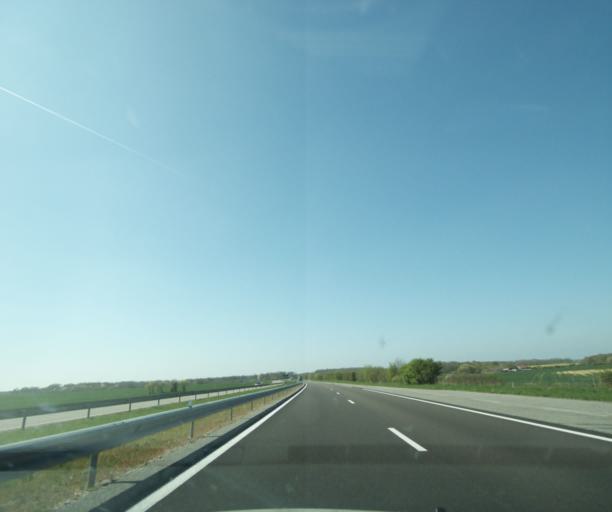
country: FR
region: Centre
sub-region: Departement du Loiret
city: Briare
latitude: 47.6333
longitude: 2.7818
